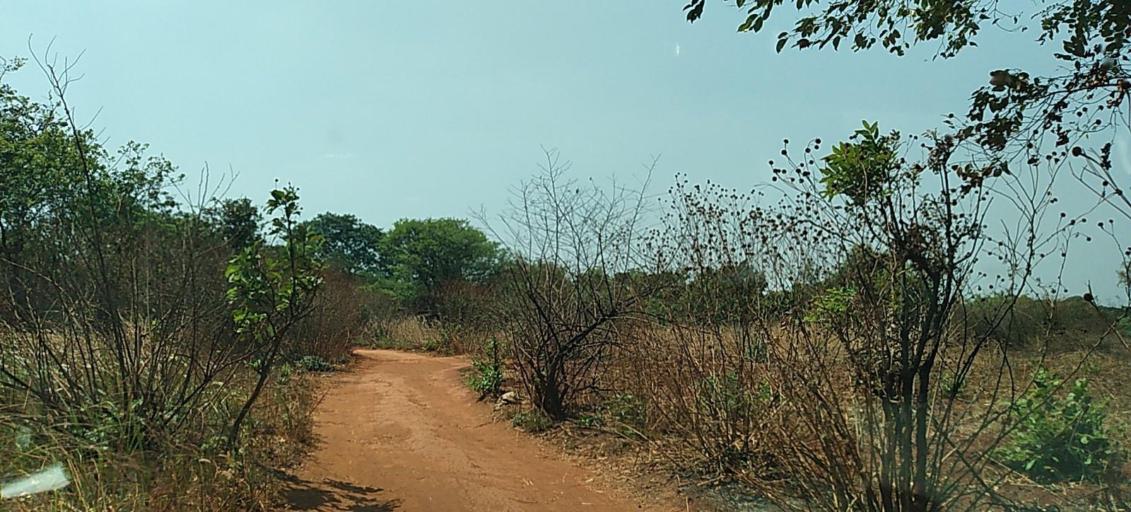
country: ZM
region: North-Western
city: Solwezi
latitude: -12.1249
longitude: 26.3056
